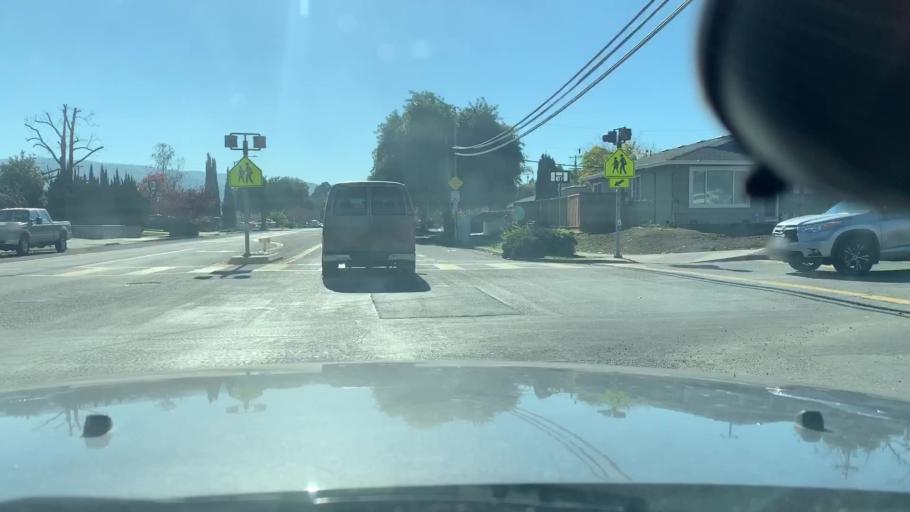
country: US
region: California
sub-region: Santa Clara County
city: Campbell
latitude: 37.2767
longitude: -121.9768
